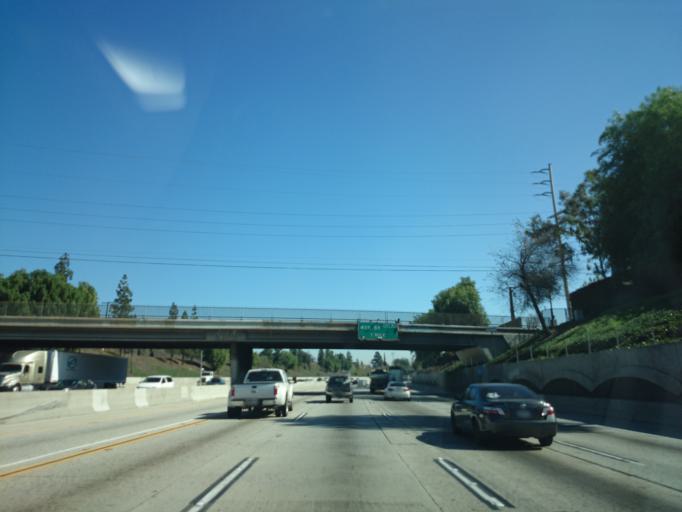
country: US
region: California
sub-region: San Bernardino County
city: Upland
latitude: 34.0870
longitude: -117.6422
